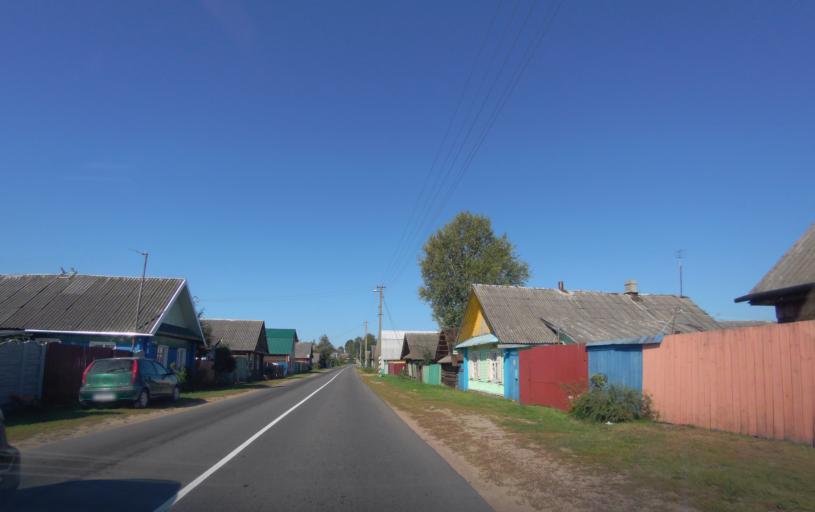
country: BY
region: Minsk
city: Horad Barysaw
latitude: 54.2569
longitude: 28.3916
